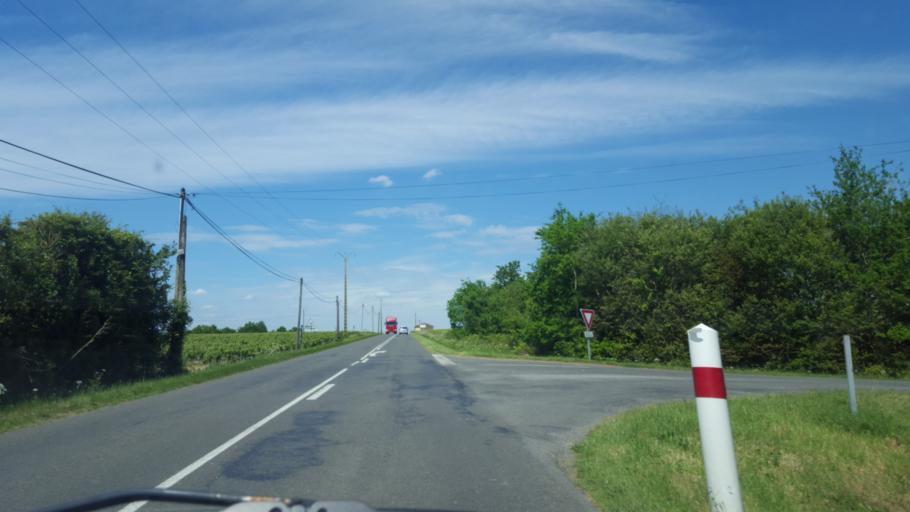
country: FR
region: Pays de la Loire
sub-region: Departement de la Loire-Atlantique
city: Saint-Philbert-de-Grand-Lieu
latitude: 47.0107
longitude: -1.6531
